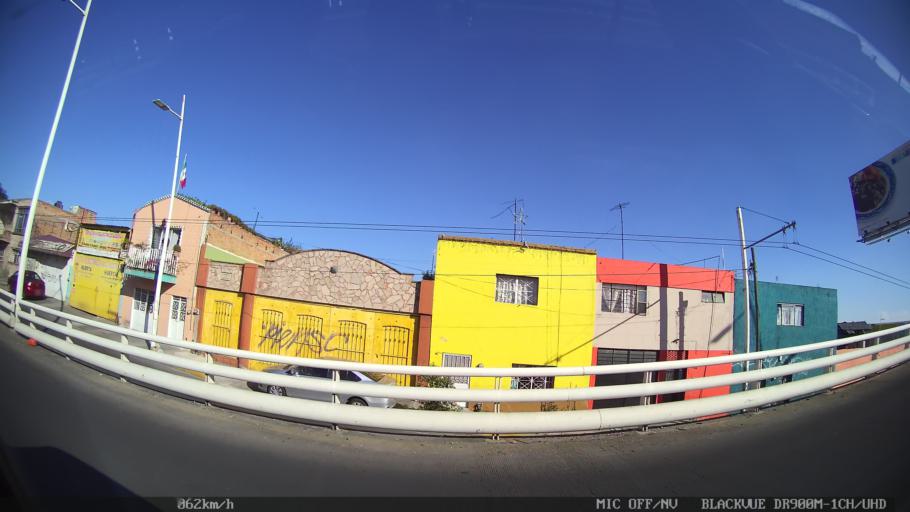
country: MX
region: Jalisco
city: Tlaquepaque
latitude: 20.6907
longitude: -103.3110
